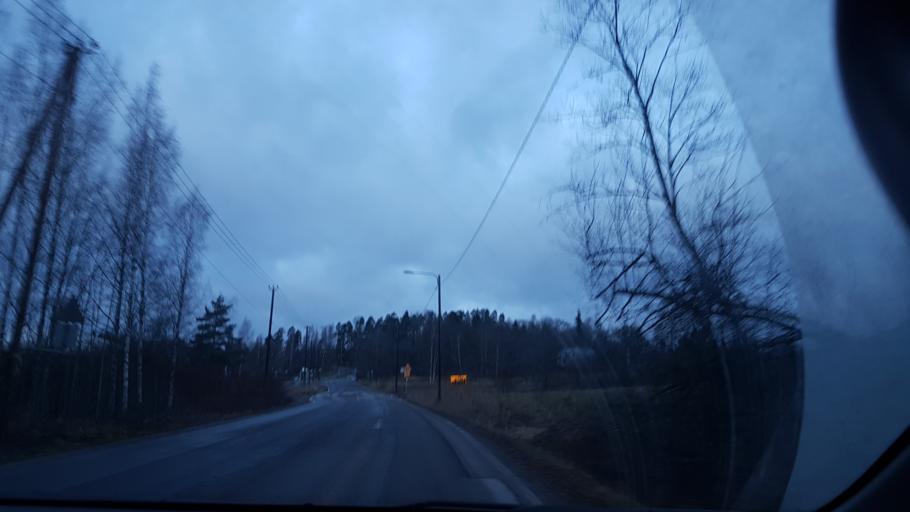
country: FI
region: Uusimaa
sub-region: Helsinki
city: Vantaa
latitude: 60.2780
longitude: 25.1269
